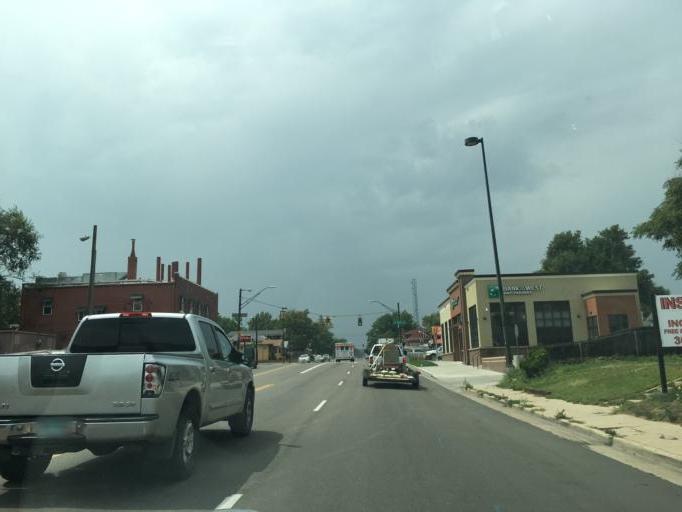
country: US
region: Colorado
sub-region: Adams County
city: Berkley
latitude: 39.7693
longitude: -105.0101
